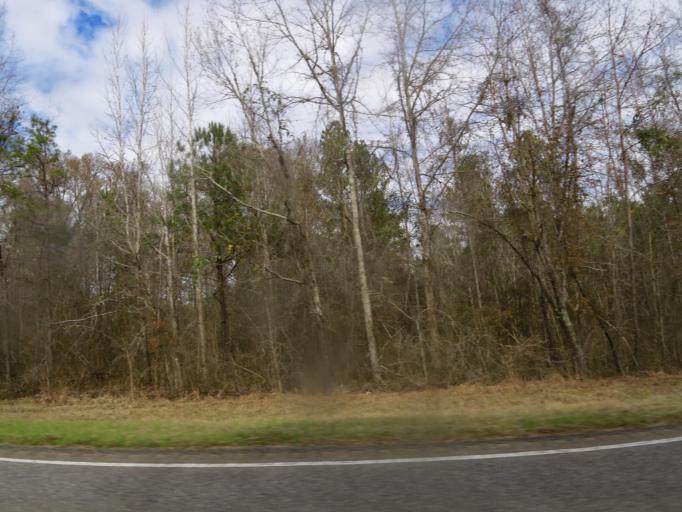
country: US
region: Alabama
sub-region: Barbour County
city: Eufaula
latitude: 31.9873
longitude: -85.2543
